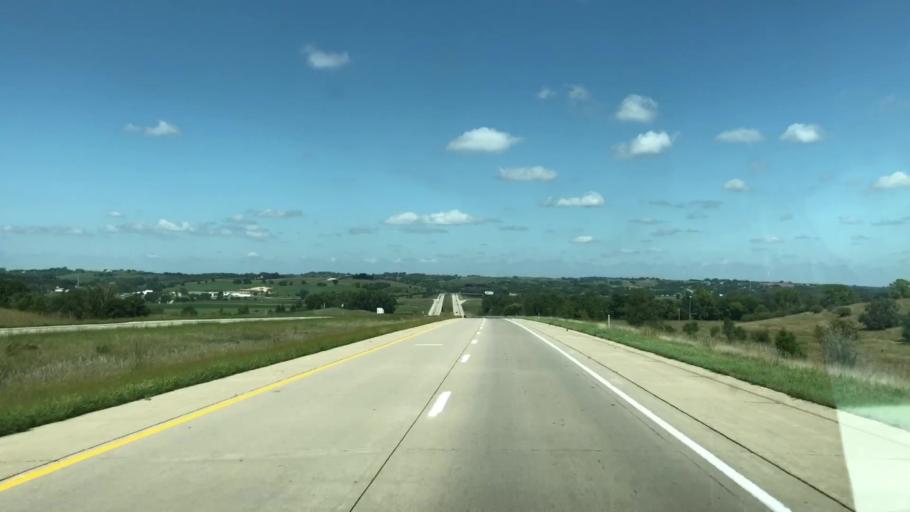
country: US
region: Iowa
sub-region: Woodbury County
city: Sioux City
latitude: 42.5349
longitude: -96.3388
